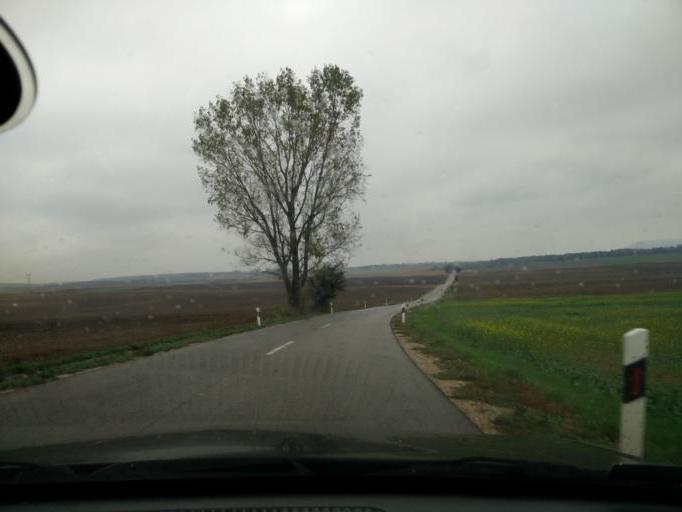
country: HU
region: Komarom-Esztergom
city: Bajna
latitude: 47.6423
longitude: 18.5713
